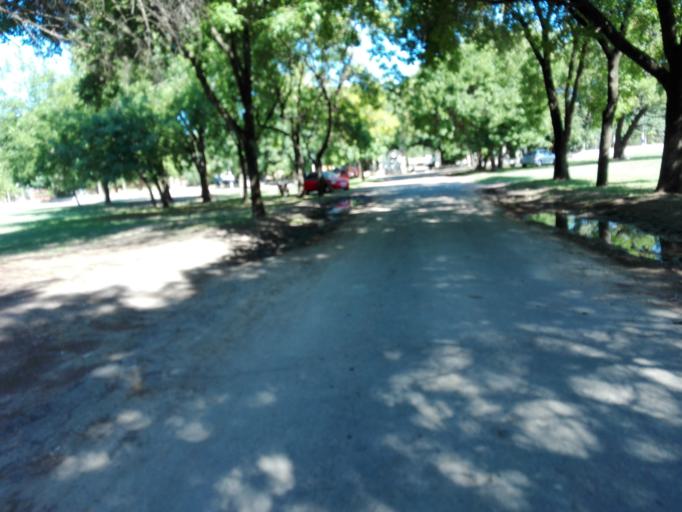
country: AR
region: Buenos Aires
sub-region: Partido de La Plata
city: La Plata
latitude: -34.9318
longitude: -57.9679
